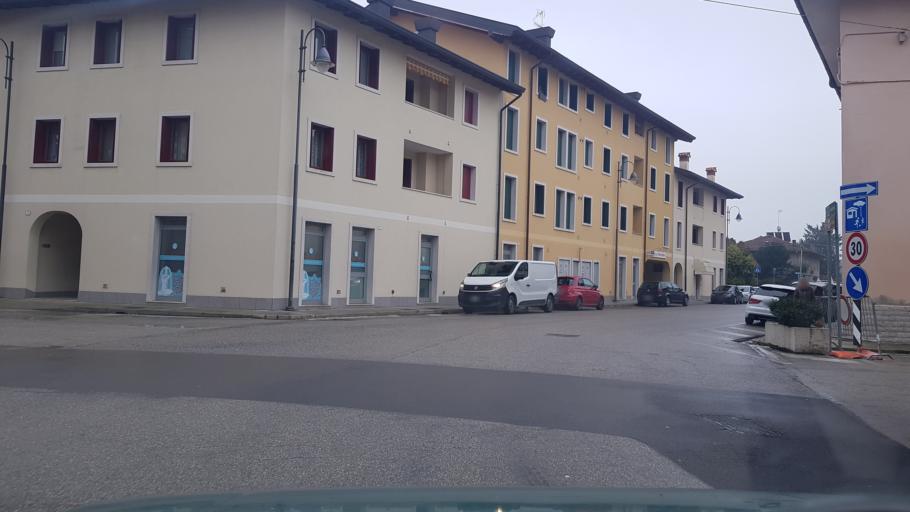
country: IT
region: Friuli Venezia Giulia
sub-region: Provincia di Udine
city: Palmanova
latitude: 45.9058
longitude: 13.3131
